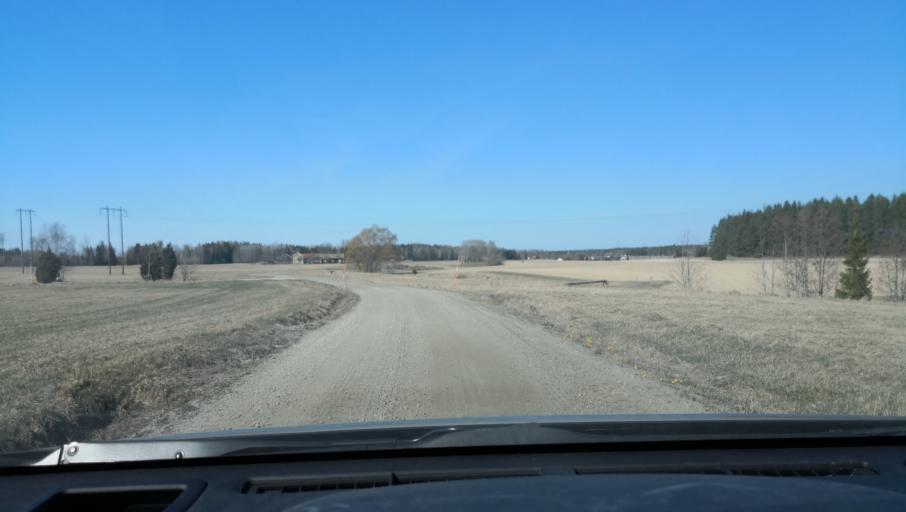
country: SE
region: Vaestmanland
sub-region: Sala Kommun
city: Sala
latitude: 59.8948
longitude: 16.5307
